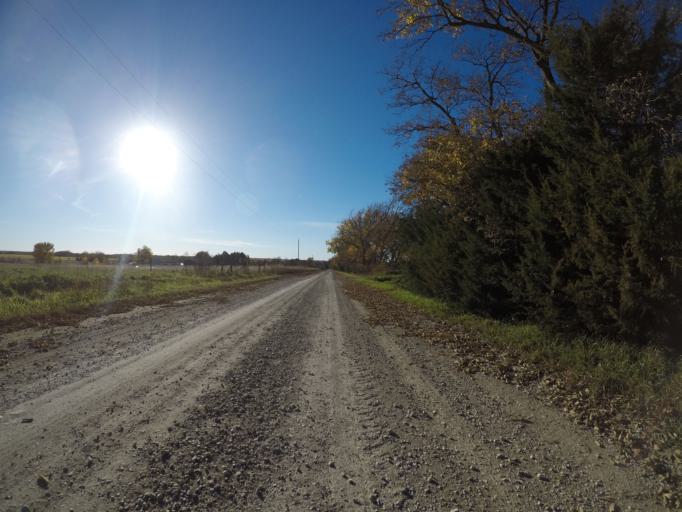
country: US
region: Kansas
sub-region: Riley County
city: Fort Riley North
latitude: 39.2620
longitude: -96.7655
